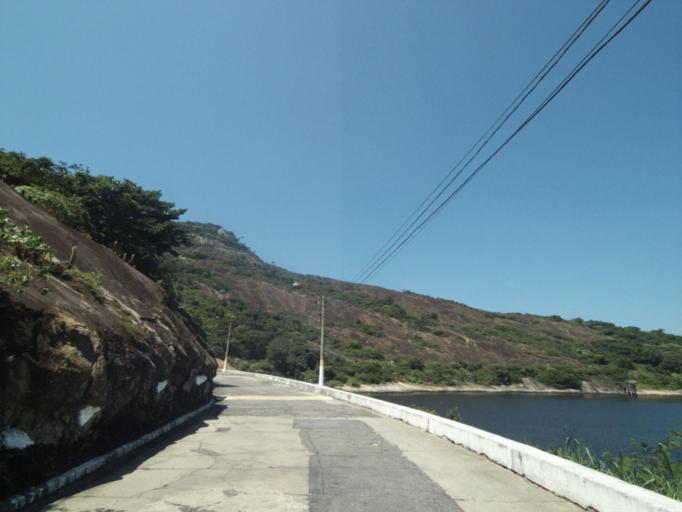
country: BR
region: Rio de Janeiro
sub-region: Niteroi
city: Niteroi
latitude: -22.9330
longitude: -43.1271
